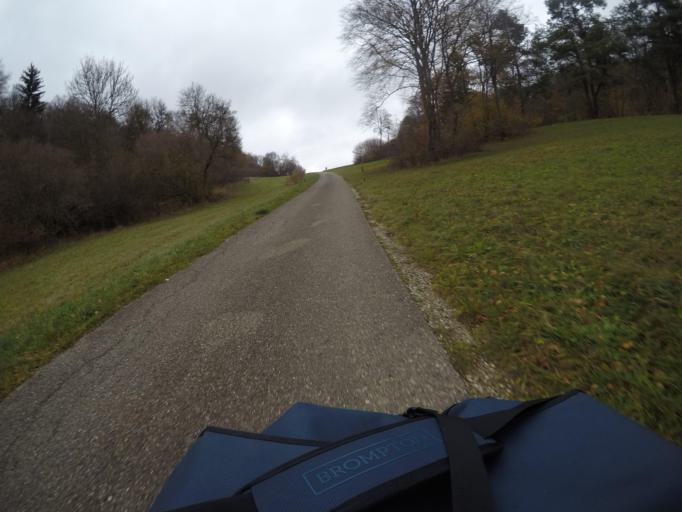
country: DE
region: Baden-Wuerttemberg
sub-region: Tuebingen Region
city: Pfullingen
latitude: 48.4028
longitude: 9.2439
